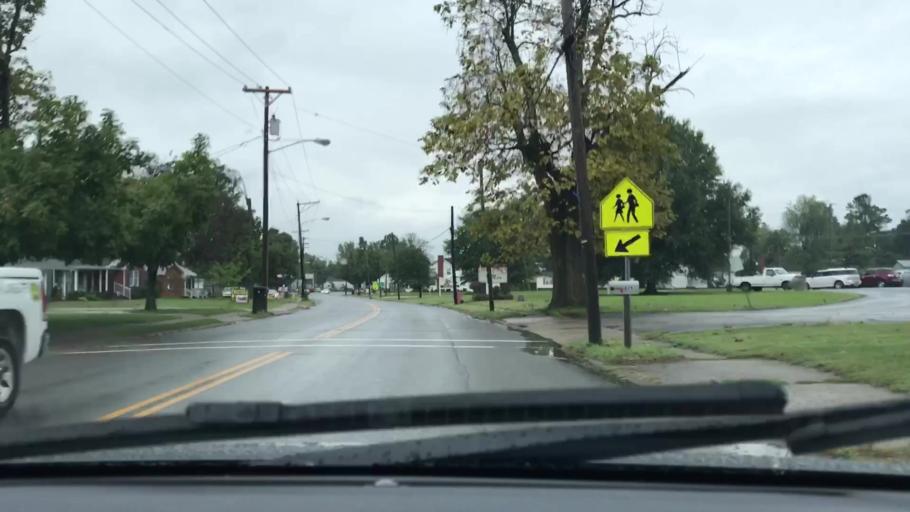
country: US
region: Kentucky
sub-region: McLean County
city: Calhoun
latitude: 37.5439
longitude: -87.2598
